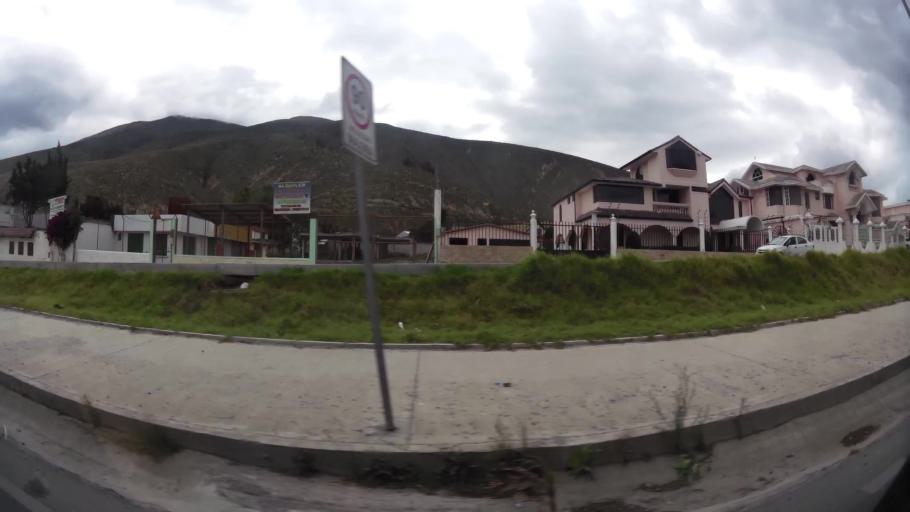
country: EC
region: Pichincha
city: Quito
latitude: -0.0138
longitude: -78.4531
